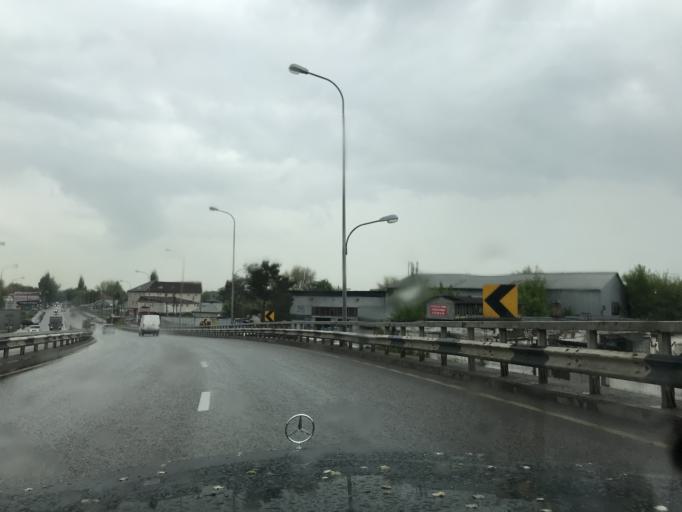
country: KZ
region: Almaty Oblysy
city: Pervomayskiy
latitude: 43.3386
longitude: 76.9655
